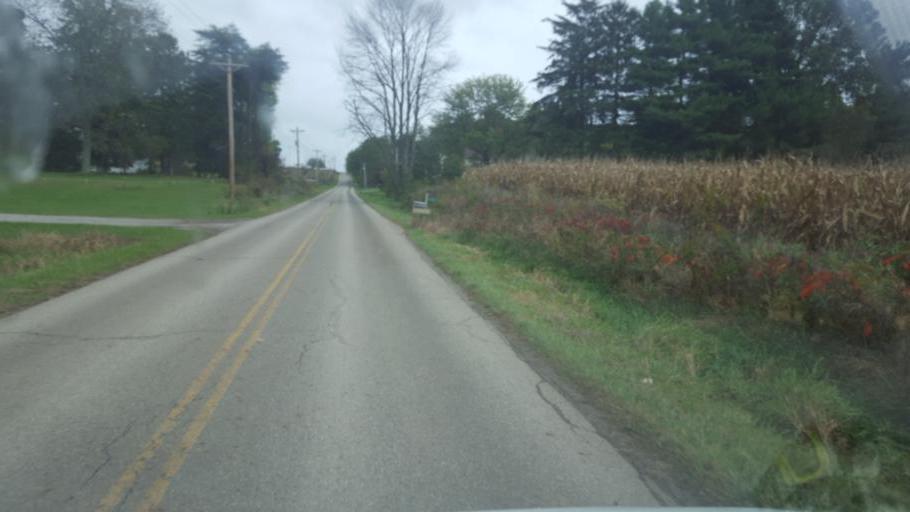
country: US
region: Ohio
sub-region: Wayne County
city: Shreve
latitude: 40.6243
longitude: -82.0651
